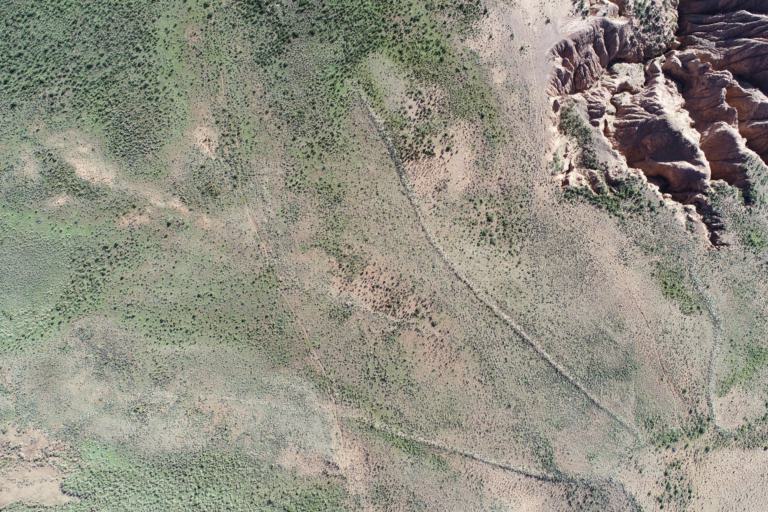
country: BO
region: La Paz
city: Curahuara de Carangas
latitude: -17.3042
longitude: -68.5012
